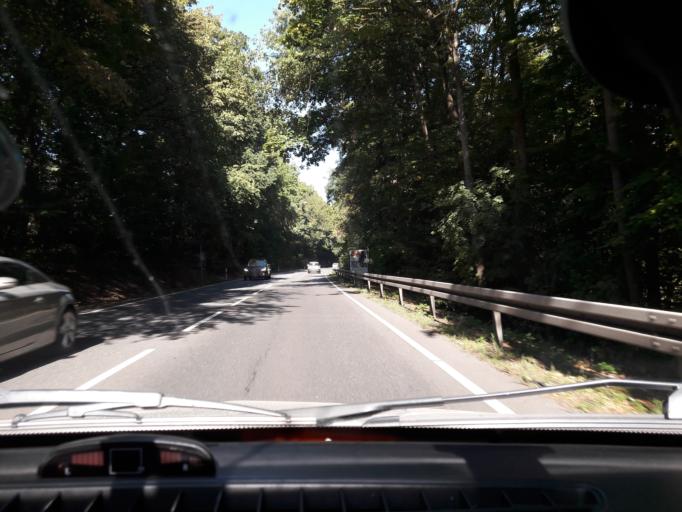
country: DE
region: Hesse
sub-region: Regierungsbezirk Darmstadt
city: Wiesbaden
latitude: 50.0926
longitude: 8.2128
